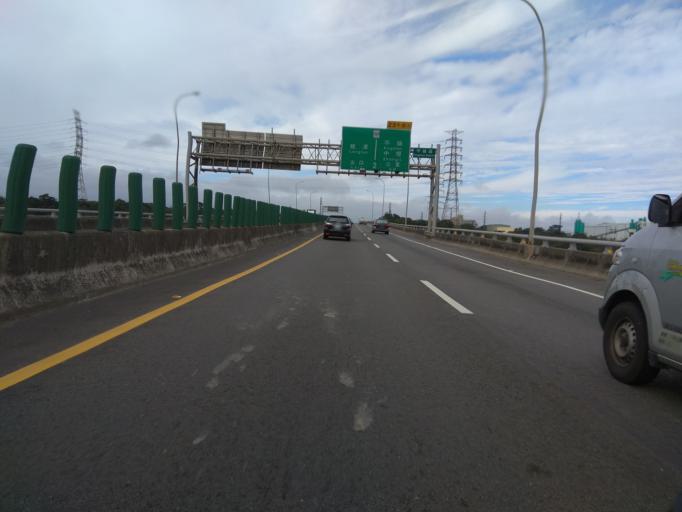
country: TW
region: Taiwan
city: Daxi
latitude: 24.8986
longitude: 121.2554
